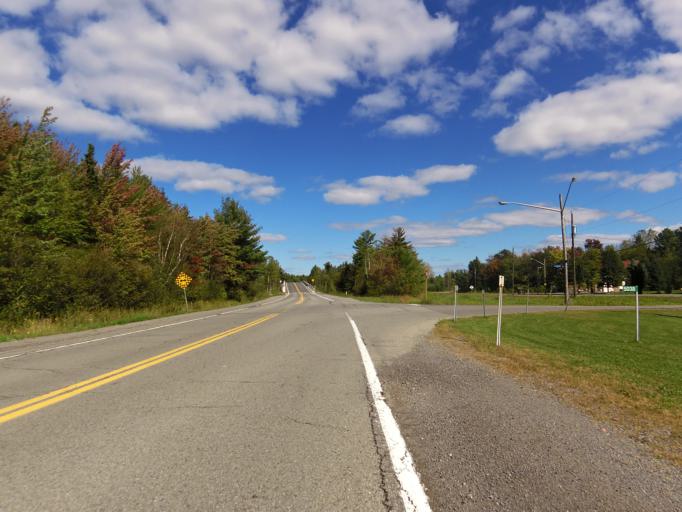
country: CA
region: Ontario
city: Ottawa
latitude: 45.3642
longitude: -75.5239
